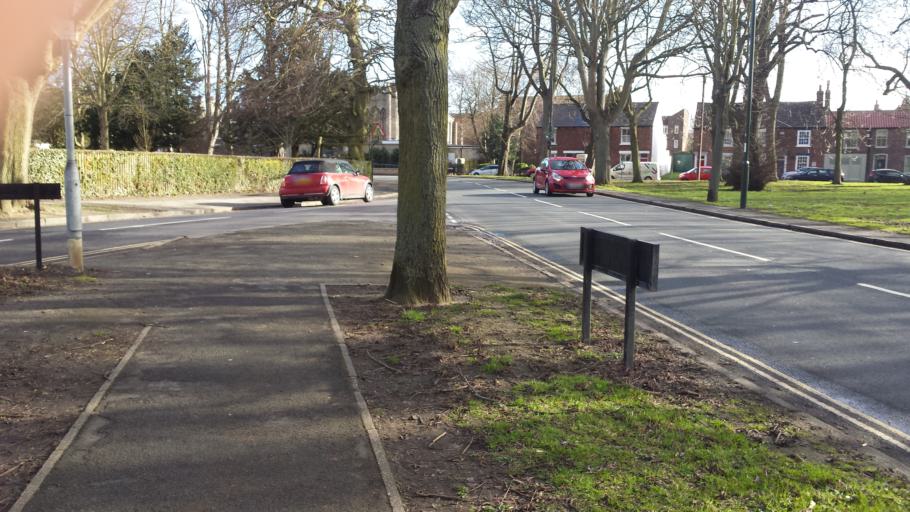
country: GB
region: England
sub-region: East Riding of Yorkshire
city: Beverley
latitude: 53.8390
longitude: -0.4320
